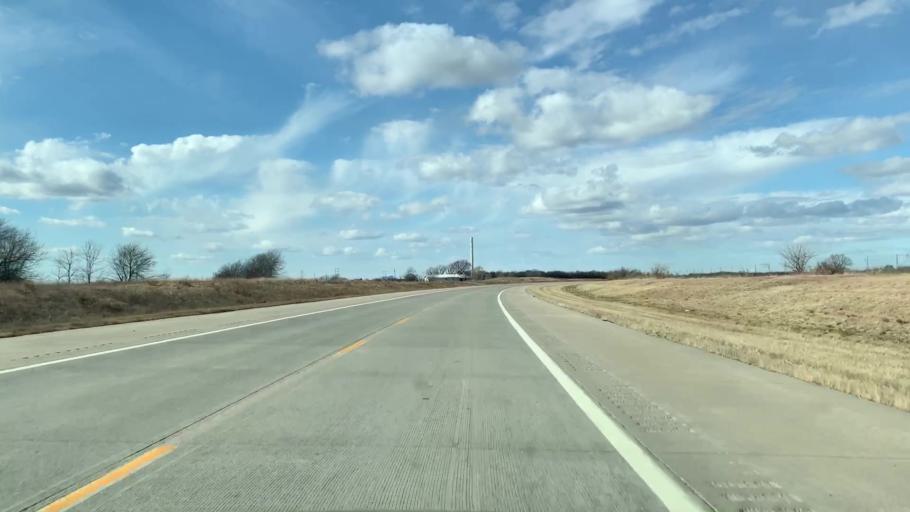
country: US
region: Kansas
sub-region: Labette County
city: Parsons
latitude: 37.3518
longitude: -95.2066
